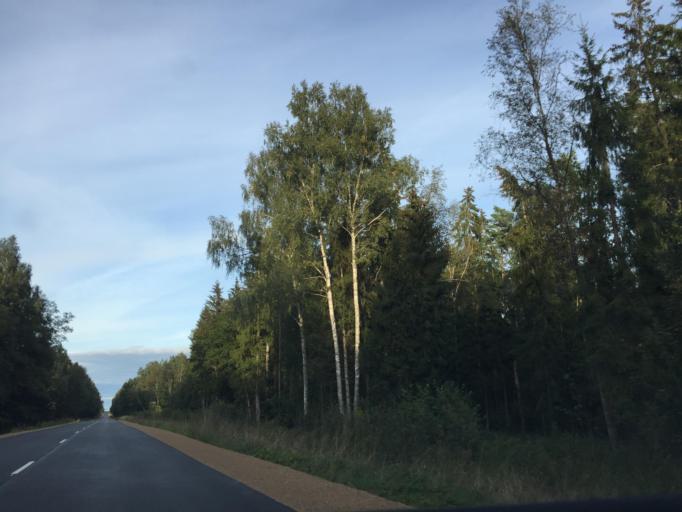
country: LV
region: Viesite
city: Viesite
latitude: 56.3462
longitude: 25.5771
